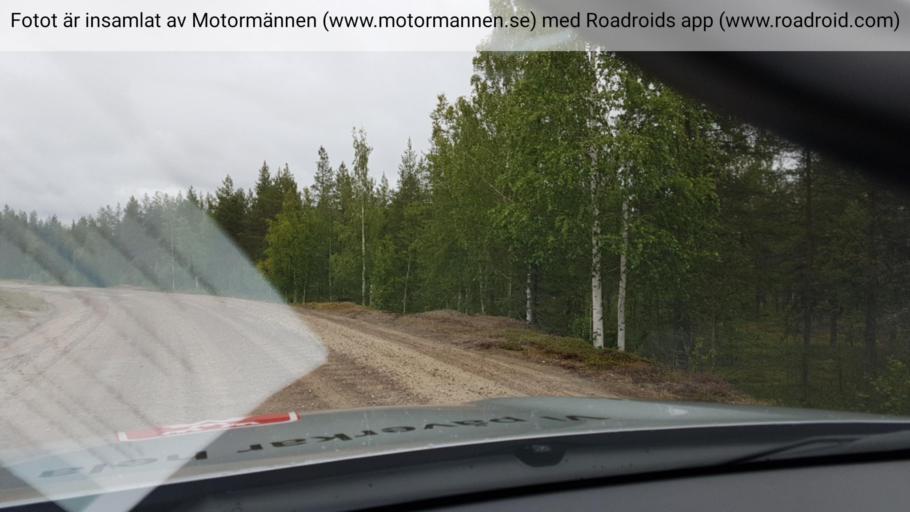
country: SE
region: Norrbotten
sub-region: Gallivare Kommun
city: Gaellivare
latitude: 66.7482
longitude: 20.9354
